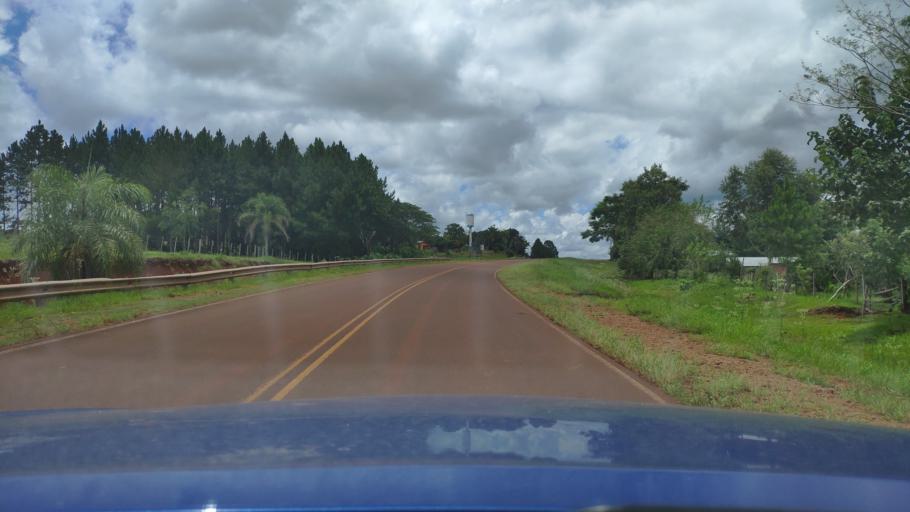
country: AR
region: Misiones
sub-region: Departamento de San Javier
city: San Javier
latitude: -27.8573
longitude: -55.2521
